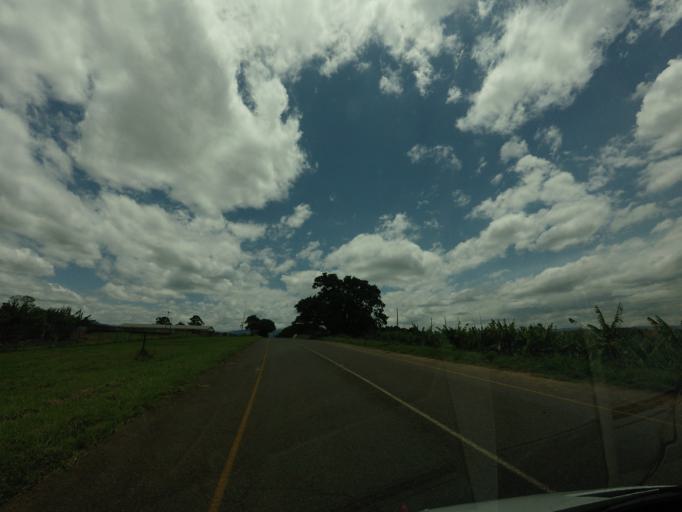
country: ZA
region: Mpumalanga
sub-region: Ehlanzeni District
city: Graksop
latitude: -25.0419
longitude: 30.9711
